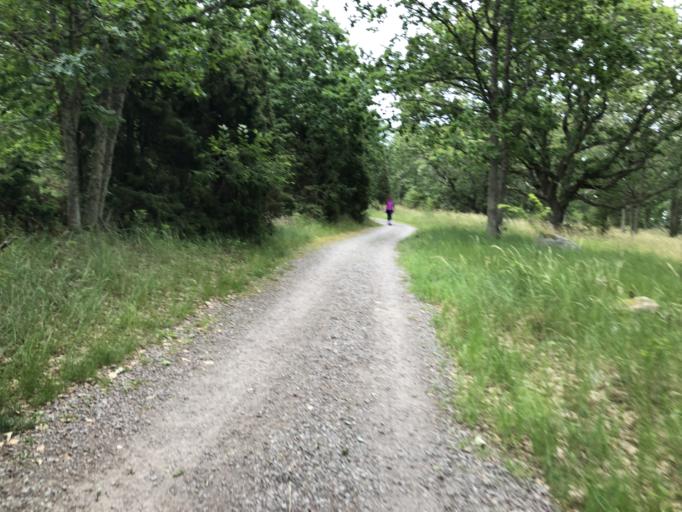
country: SE
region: Kalmar
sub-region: Kalmar Kommun
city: Kalmar
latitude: 56.6335
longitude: 16.3183
